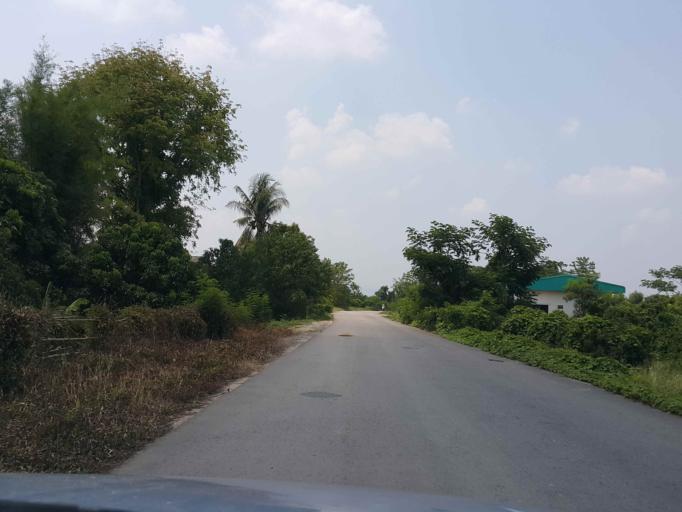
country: TH
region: Chiang Mai
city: Saraphi
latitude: 18.6776
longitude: 99.0060
